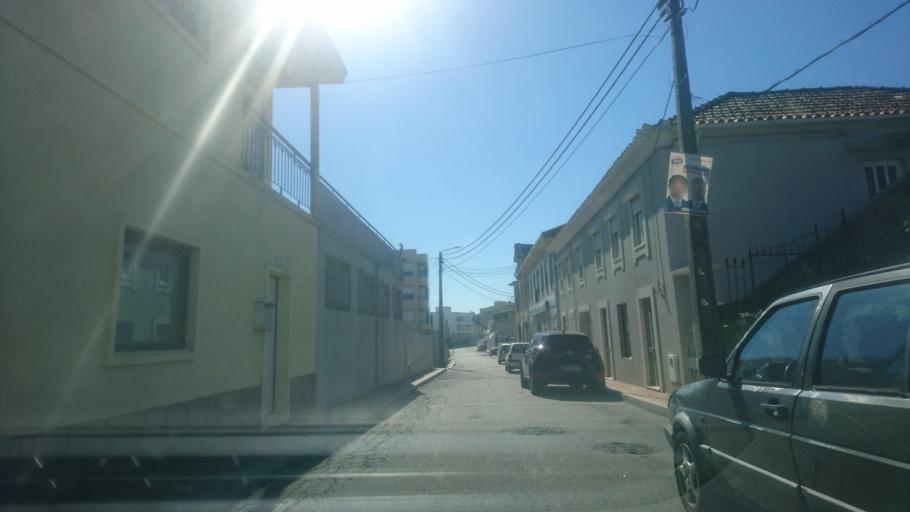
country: PT
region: Aveiro
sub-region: Santa Maria da Feira
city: Lamas
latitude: 40.9841
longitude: -8.5698
